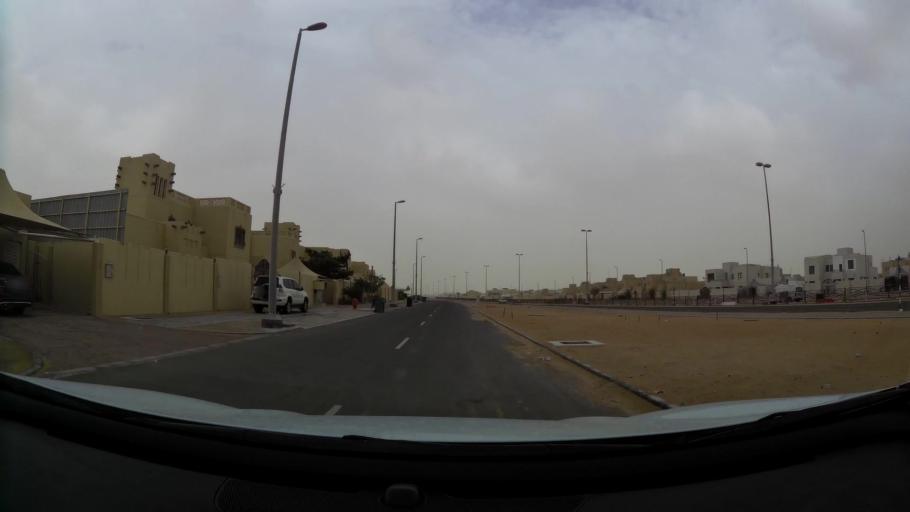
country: AE
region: Abu Dhabi
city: Abu Dhabi
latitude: 24.4505
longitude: 54.7192
